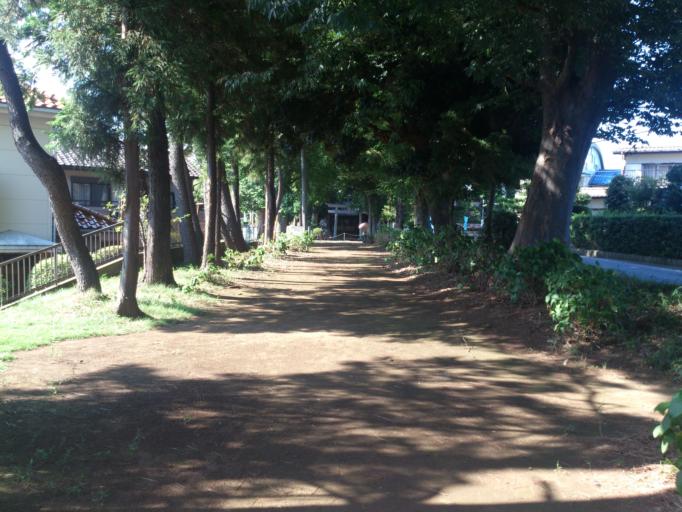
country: JP
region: Chiba
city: Matsudo
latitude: 35.7916
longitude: 139.9171
